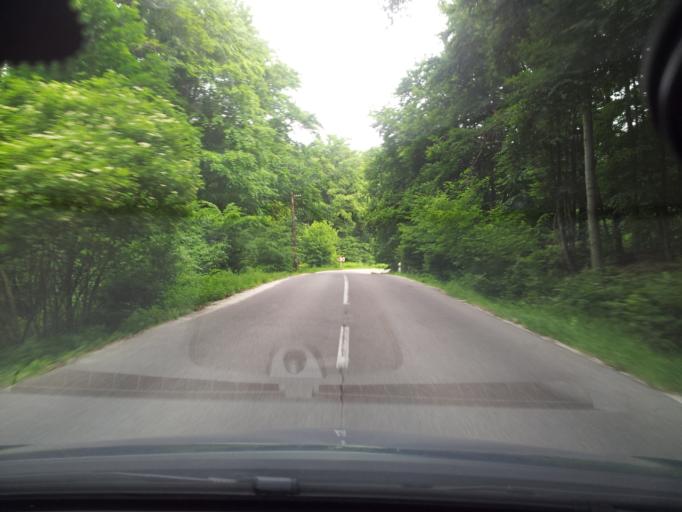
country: SK
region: Nitriansky
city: Partizanske
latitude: 48.5346
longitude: 18.4421
